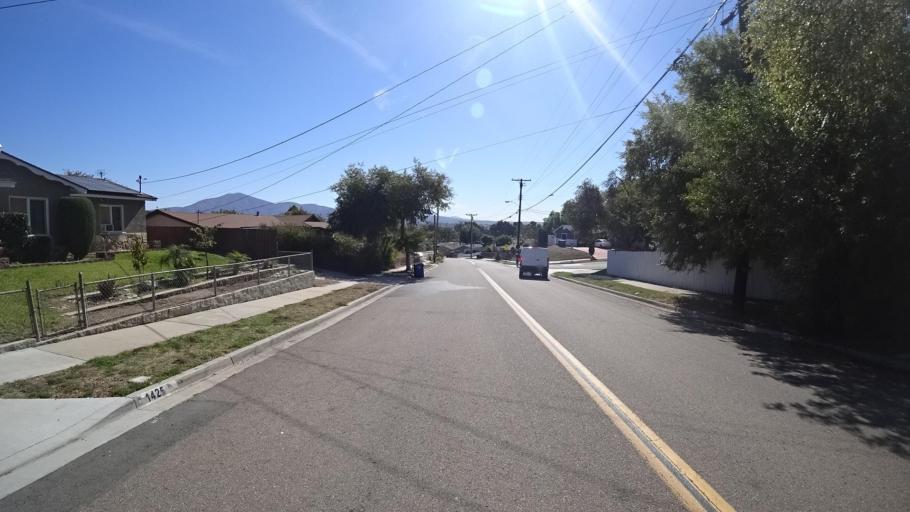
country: US
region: California
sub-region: San Diego County
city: Lemon Grove
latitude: 32.7207
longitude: -117.0192
